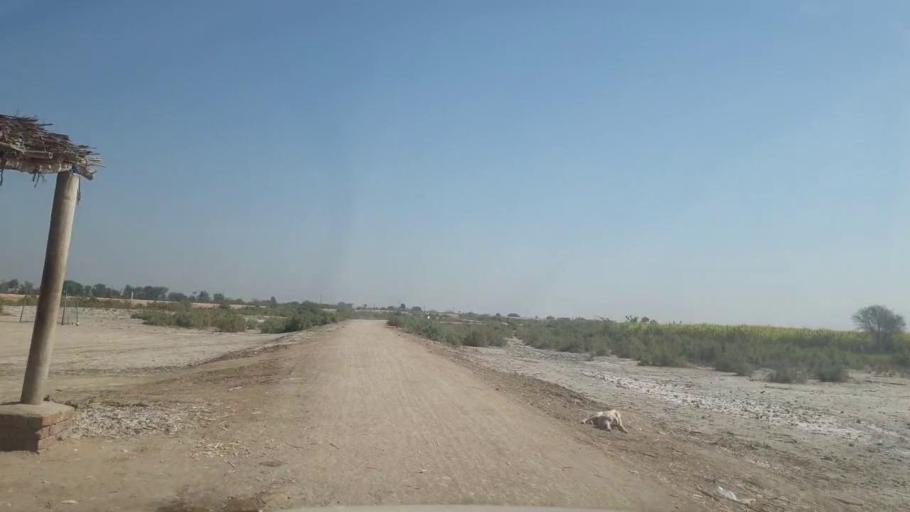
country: PK
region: Sindh
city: Mirpur Khas
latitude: 25.5193
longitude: 69.1837
